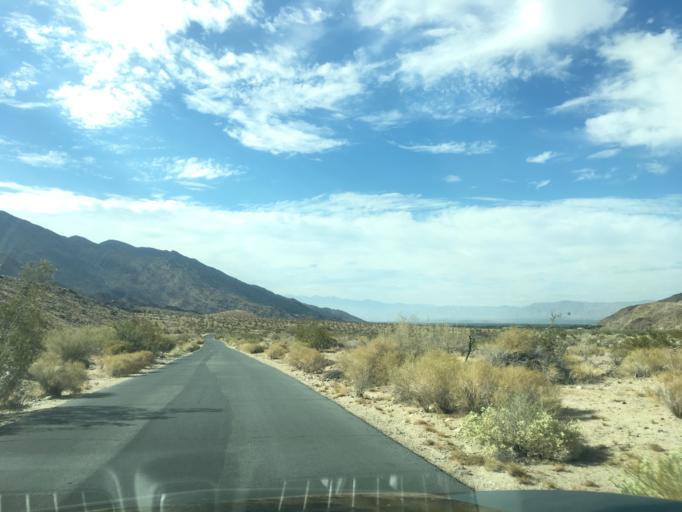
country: US
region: California
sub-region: Riverside County
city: Cathedral City
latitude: 33.7469
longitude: -116.5378
